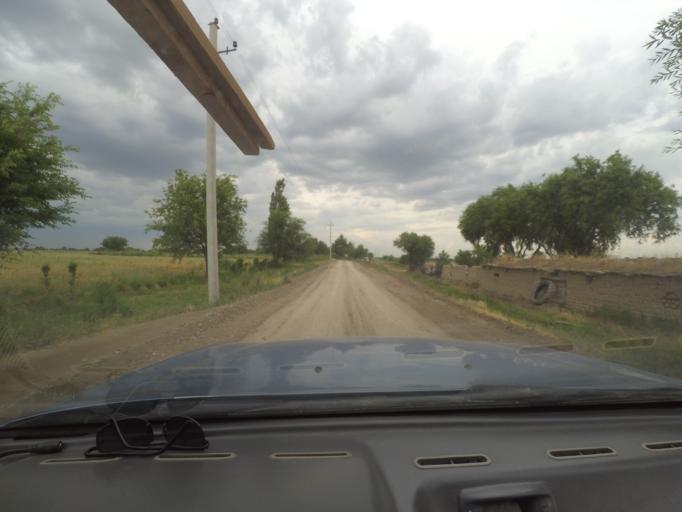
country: TJ
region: Viloyati Sughd
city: Buston
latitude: 40.5473
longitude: 69.0785
